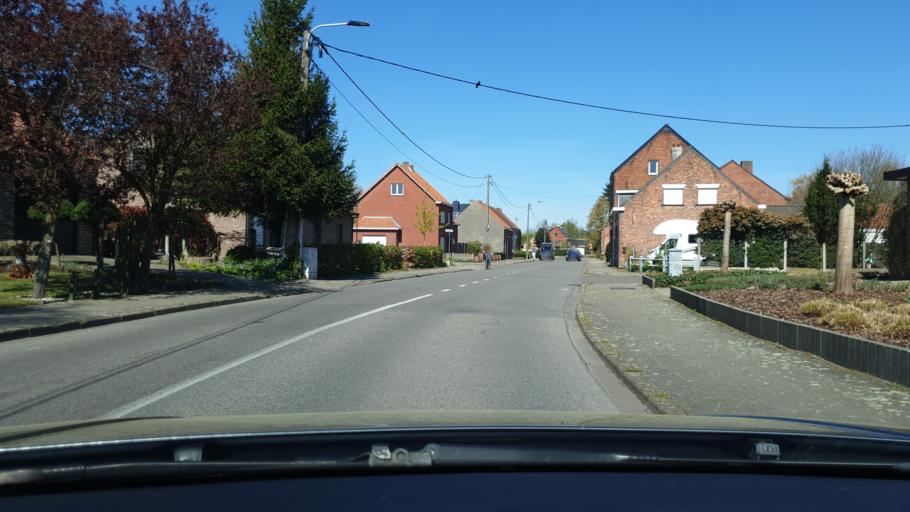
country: BE
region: Flanders
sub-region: Provincie Antwerpen
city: Geel
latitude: 51.1654
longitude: 4.9719
